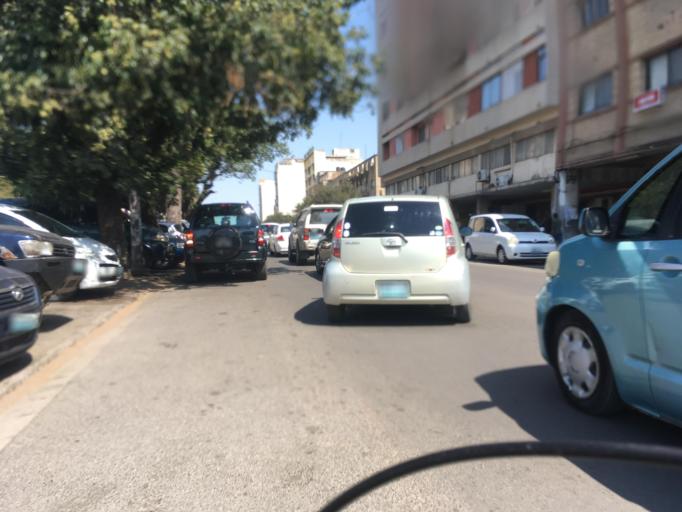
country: MZ
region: Maputo City
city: Maputo
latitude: -25.9618
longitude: 32.5740
